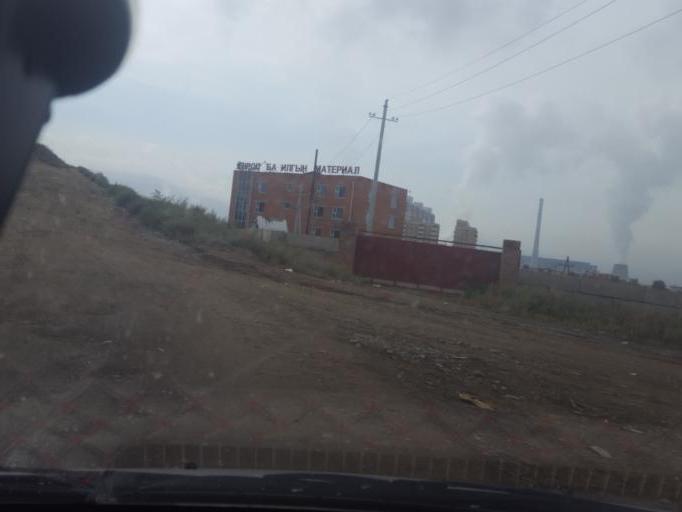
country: MN
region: Ulaanbaatar
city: Ulaanbaatar
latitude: 47.9155
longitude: 106.8005
